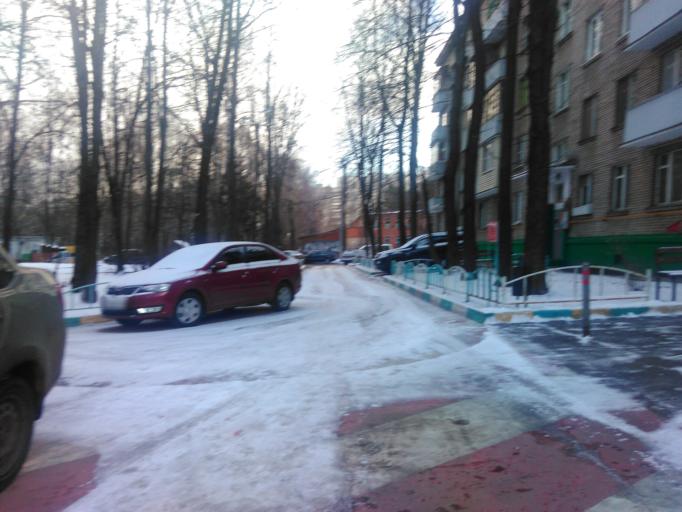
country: RU
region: Moscow
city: Tsaritsyno
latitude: 55.6476
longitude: 37.6497
